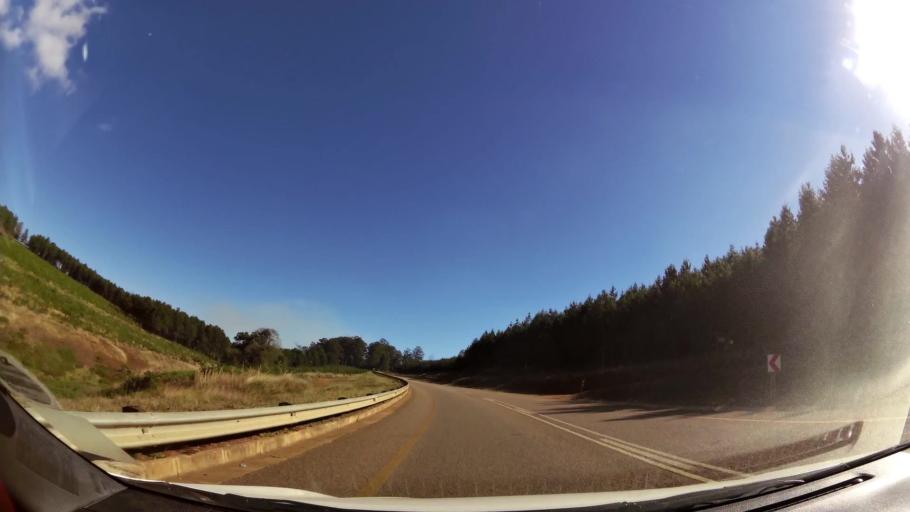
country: ZA
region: Limpopo
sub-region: Capricorn District Municipality
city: Mankoeng
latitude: -23.9110
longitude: 29.9675
